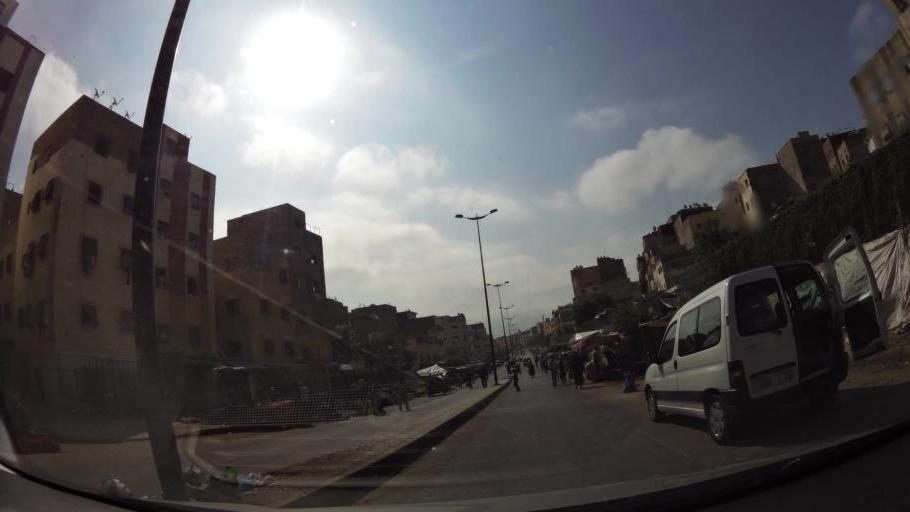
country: MA
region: Fes-Boulemane
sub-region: Fes
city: Fes
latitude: 34.0684
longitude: -5.0074
